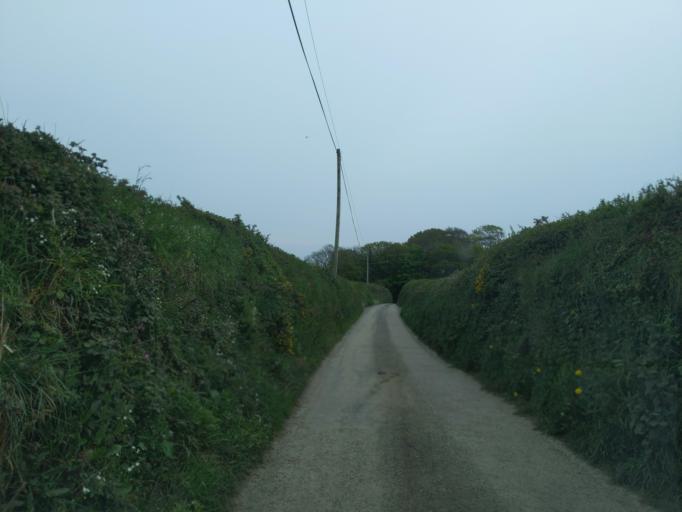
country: GB
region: England
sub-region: Cornwall
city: St Austell
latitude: 50.3093
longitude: -4.7656
